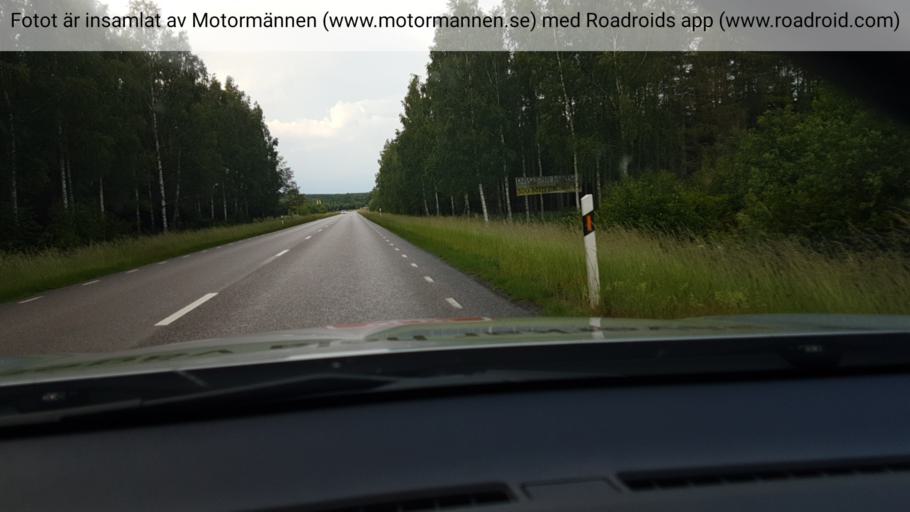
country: SE
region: Vaestra Goetaland
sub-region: Hjo Kommun
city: Hjo
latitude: 58.2454
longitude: 14.2303
